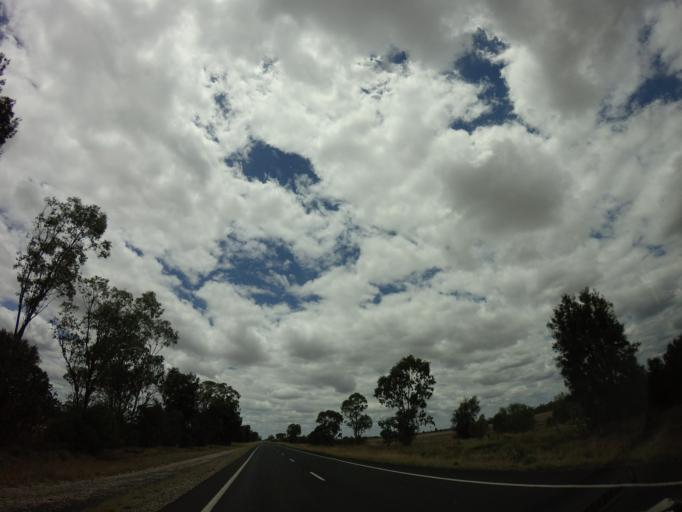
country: AU
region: Queensland
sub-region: Goondiwindi
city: Goondiwindi
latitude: -28.1767
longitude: 150.4773
